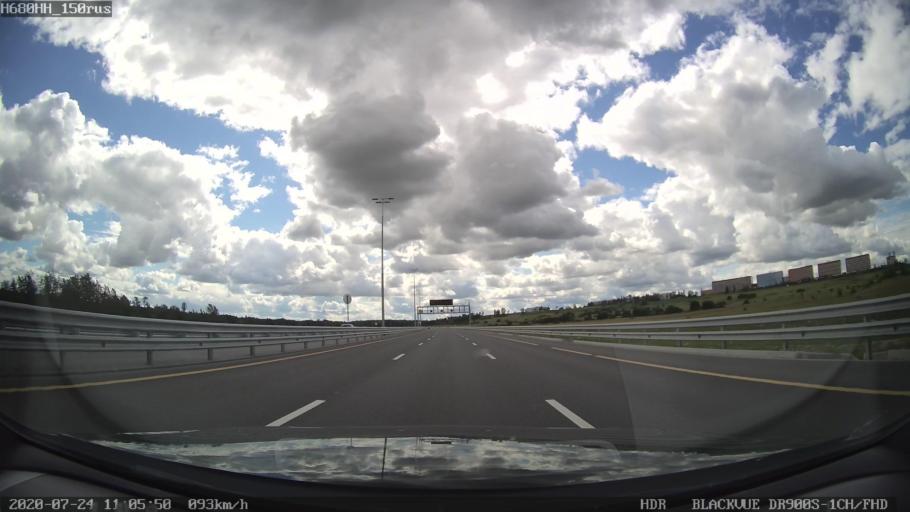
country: RU
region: St.-Petersburg
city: Shushary
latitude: 59.7718
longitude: 30.3627
